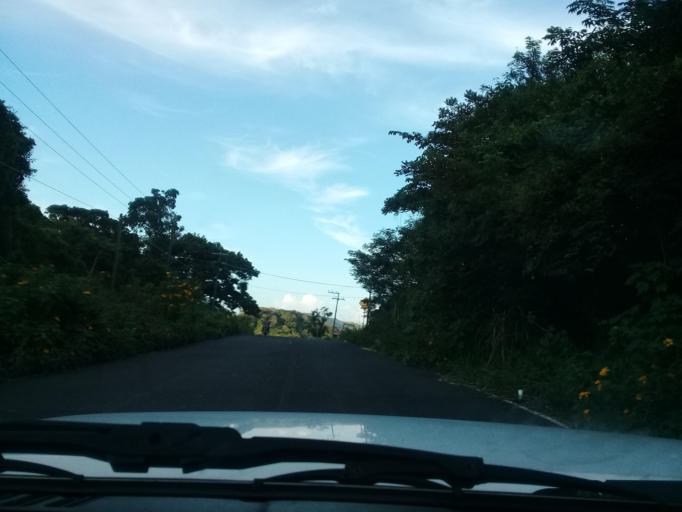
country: MX
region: Veracruz
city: Catemaco
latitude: 18.4368
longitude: -95.0891
